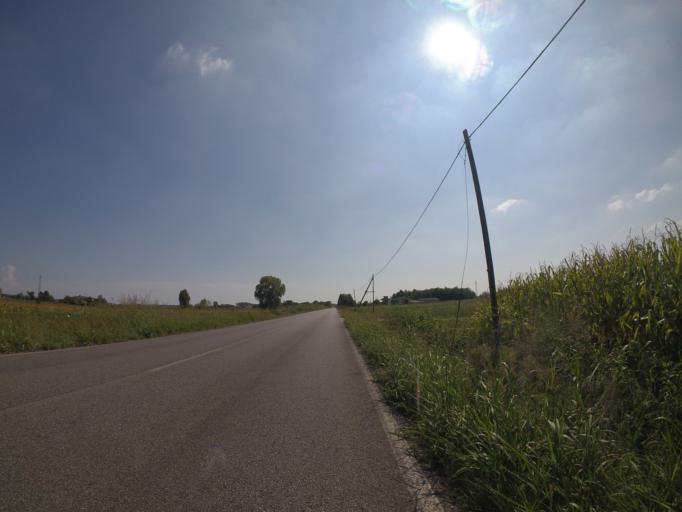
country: IT
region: Friuli Venezia Giulia
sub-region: Provincia di Udine
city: Pocenia
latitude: 45.8160
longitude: 13.1017
